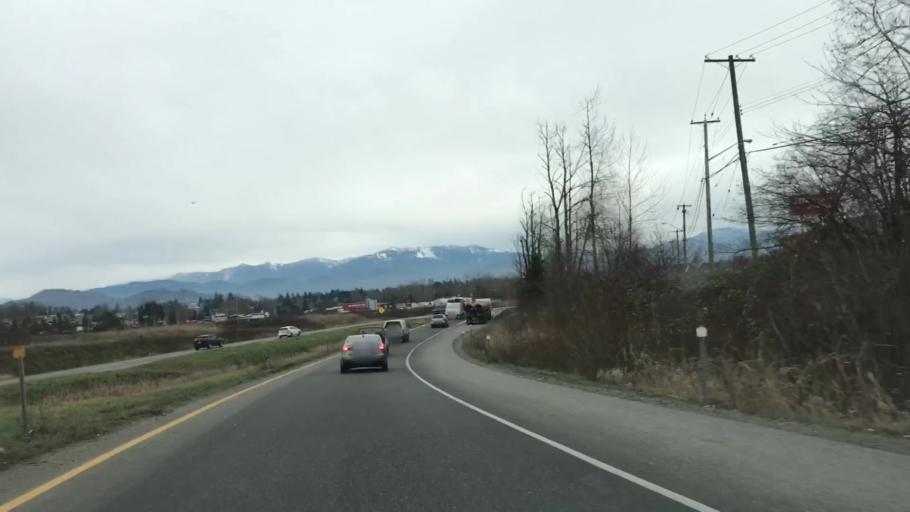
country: CA
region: British Columbia
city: Aldergrove
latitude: 49.0554
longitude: -122.3771
